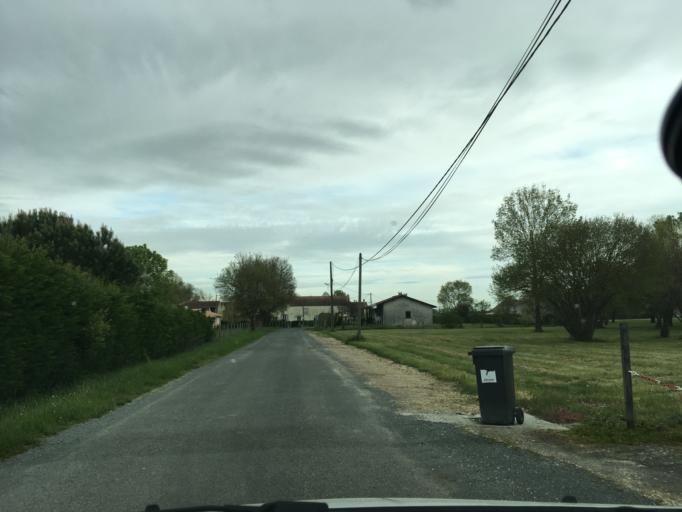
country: FR
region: Aquitaine
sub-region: Departement de la Gironde
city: Lesparre-Medoc
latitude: 45.3106
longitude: -0.8935
